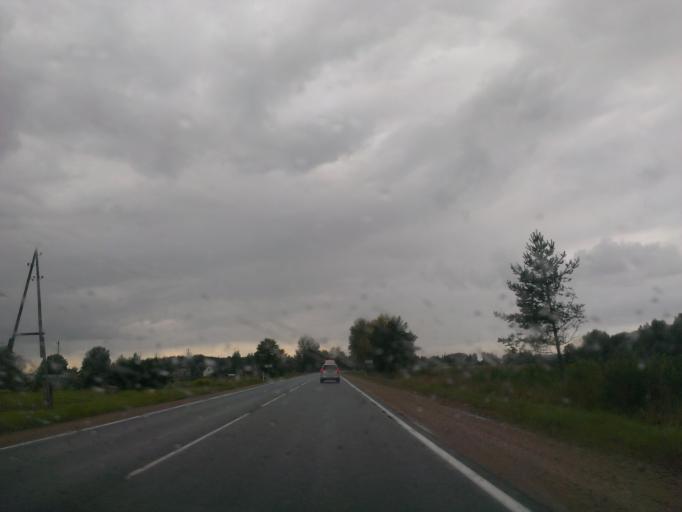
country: LV
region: Ogre
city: Ogre
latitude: 56.7745
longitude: 24.6610
